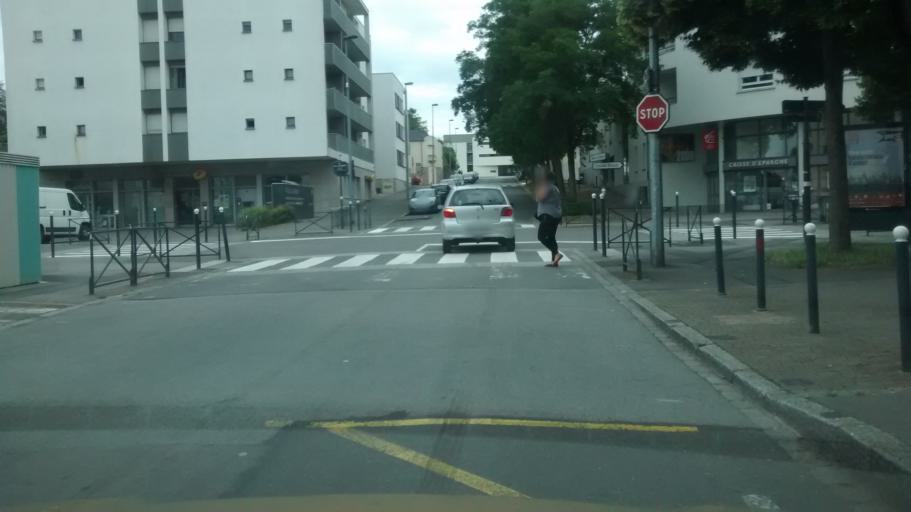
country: FR
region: Brittany
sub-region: Departement d'Ille-et-Vilaine
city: Rennes
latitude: 48.1007
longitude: -1.7069
